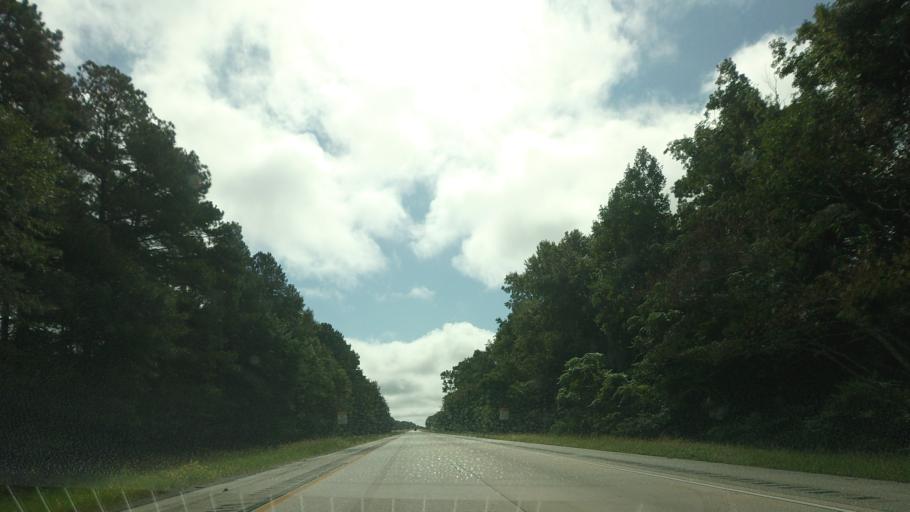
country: US
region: Georgia
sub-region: Twiggs County
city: Jeffersonville
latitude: 32.6172
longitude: -83.3556
